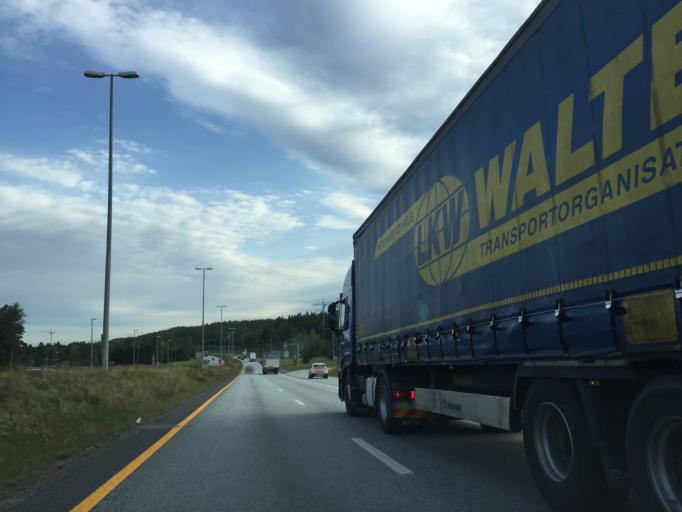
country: NO
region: Akershus
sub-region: Oppegard
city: Kolbotn
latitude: 59.7923
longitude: 10.8409
